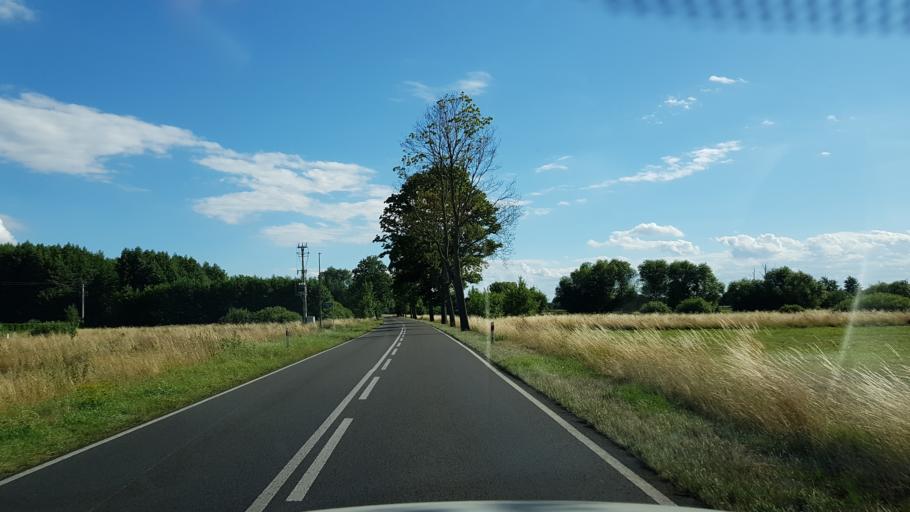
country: PL
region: West Pomeranian Voivodeship
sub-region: Powiat goleniowski
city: Goleniow
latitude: 53.5893
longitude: 14.7404
